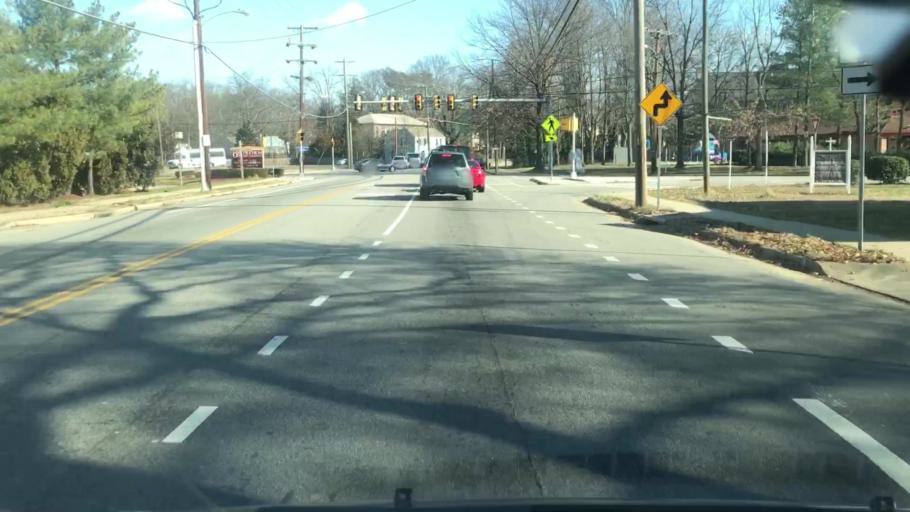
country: US
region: Virginia
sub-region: Fairfax County
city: Hybla Valley
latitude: 38.7432
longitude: -77.0818
